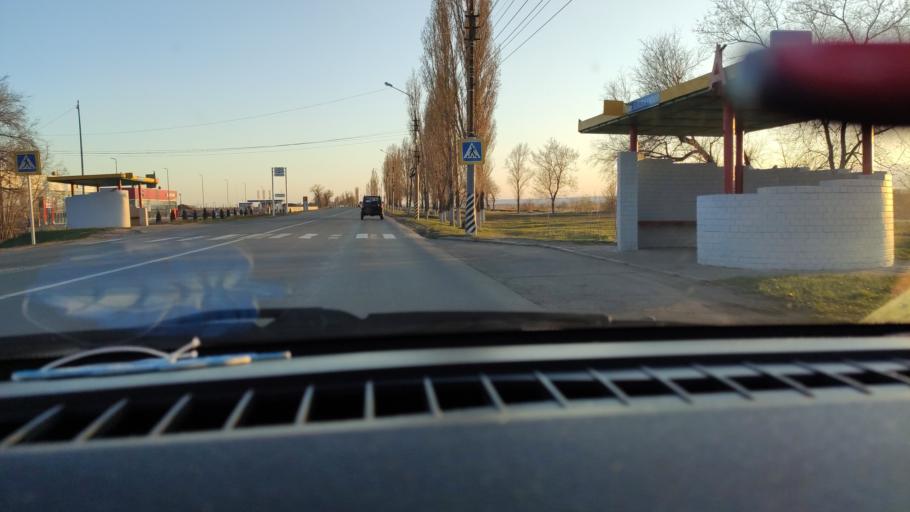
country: RU
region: Saratov
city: Privolzhskiy
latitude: 51.4419
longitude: 46.0690
